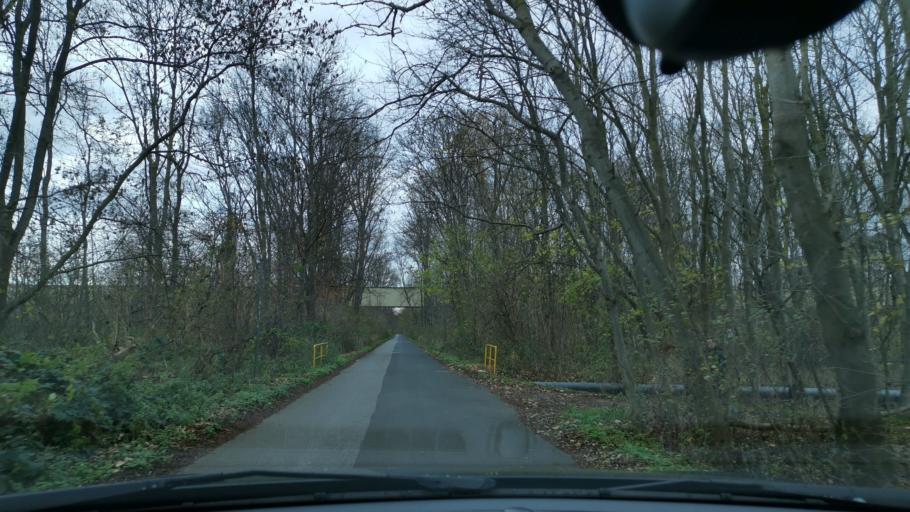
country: DE
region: North Rhine-Westphalia
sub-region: Regierungsbezirk Dusseldorf
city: Grevenbroich
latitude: 51.0535
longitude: 6.5691
